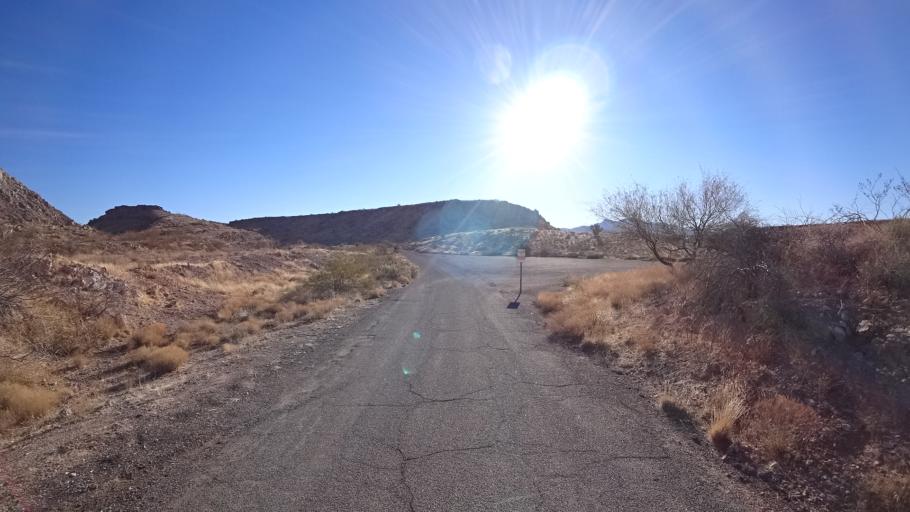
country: US
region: Arizona
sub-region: Mohave County
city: Kingman
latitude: 35.1842
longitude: -114.0366
